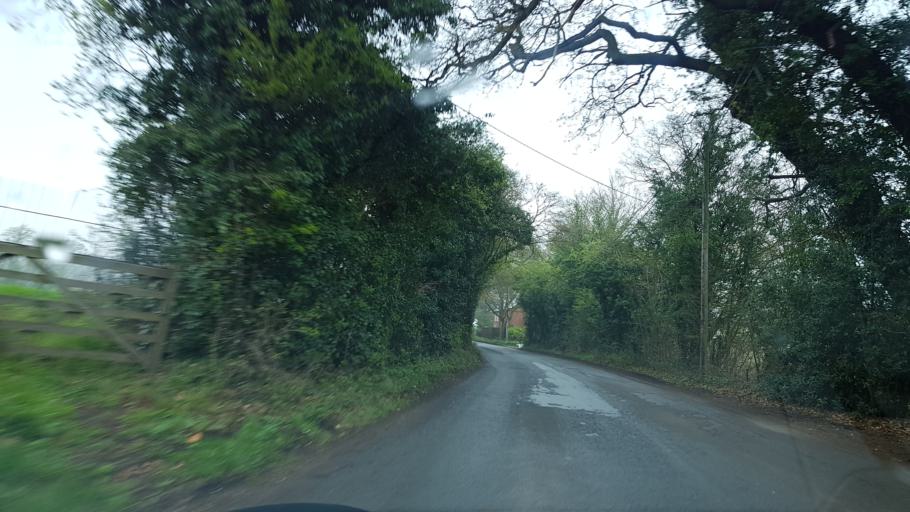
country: GB
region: England
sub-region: Herefordshire
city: Ledbury
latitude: 52.0506
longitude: -2.4257
